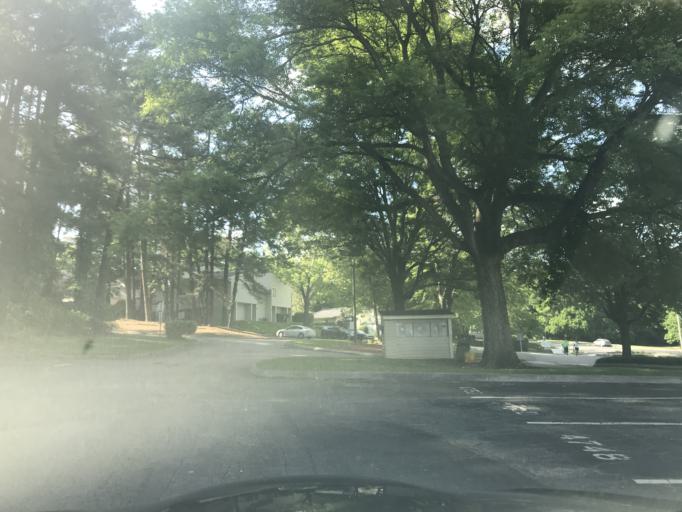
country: US
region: North Carolina
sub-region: Wake County
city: Raleigh
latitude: 35.8460
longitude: -78.5952
